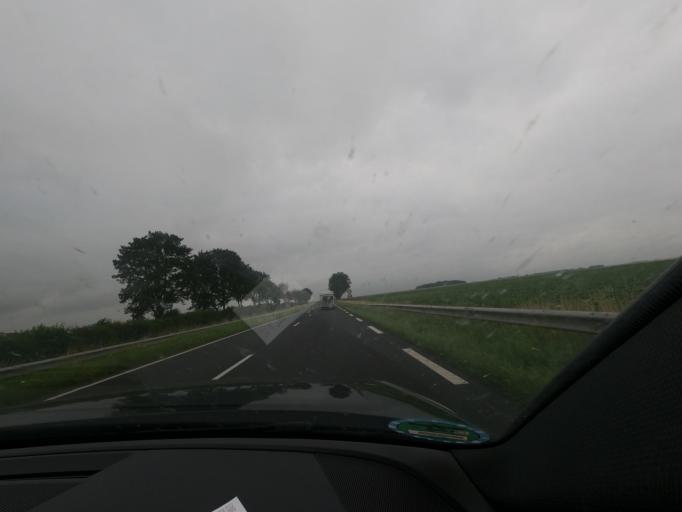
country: FR
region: Picardie
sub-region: Departement de la Somme
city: Rosieres-en-Santerre
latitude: 49.7397
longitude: 2.6891
